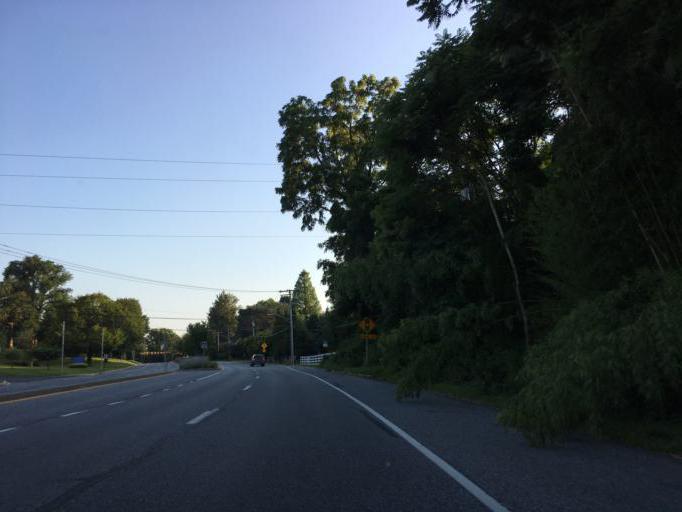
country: US
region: Maryland
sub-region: Baltimore County
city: Towson
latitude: 39.3852
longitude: -76.6259
